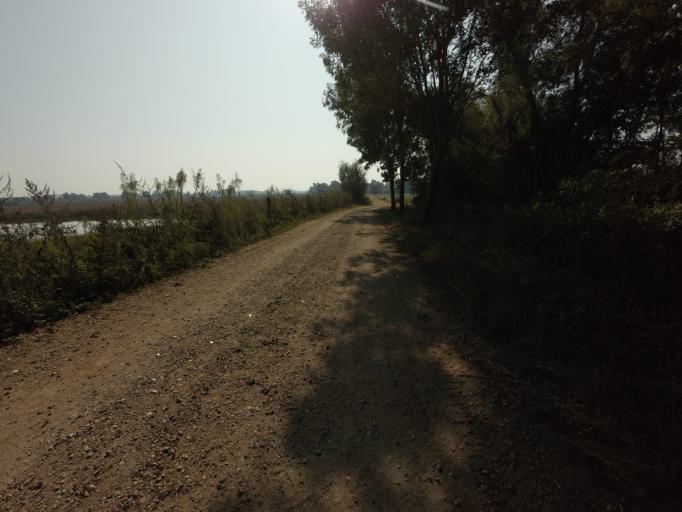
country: NL
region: Limburg
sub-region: Gemeente Roermond
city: Leeuwen
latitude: 51.2429
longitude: 5.9999
